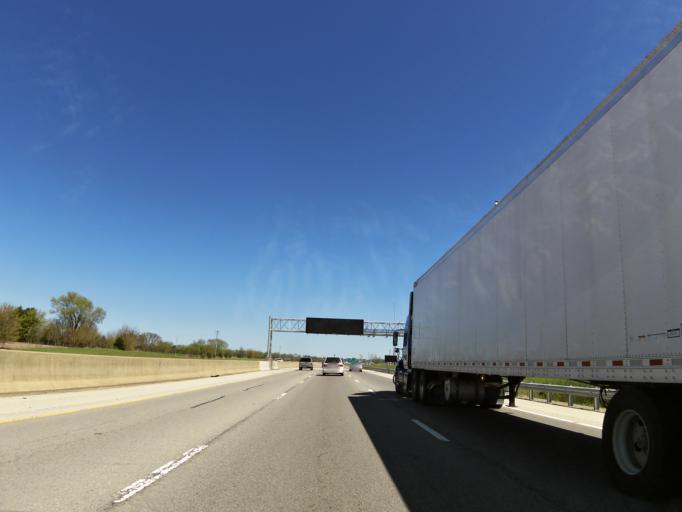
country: US
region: Kentucky
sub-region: Edmonson County
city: Brownsville
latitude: 37.0386
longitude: -86.2285
